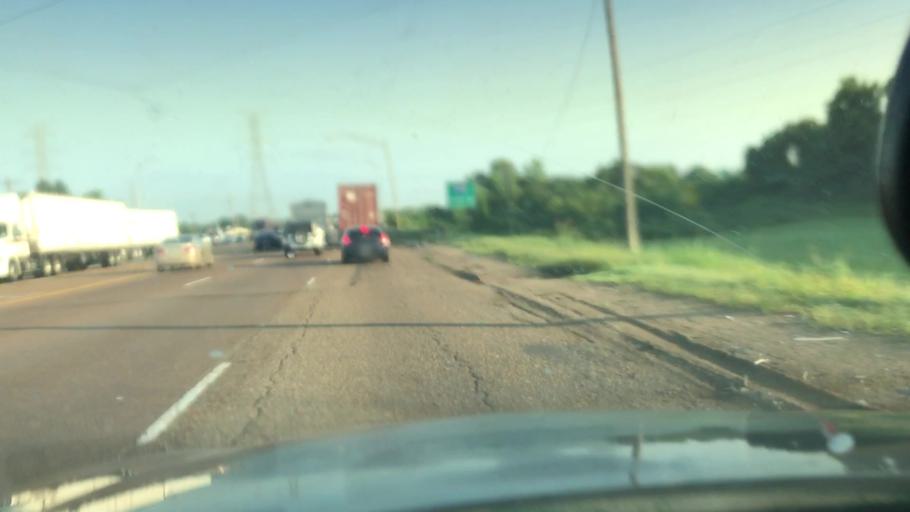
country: US
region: Tennessee
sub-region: Shelby County
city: New South Memphis
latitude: 35.0772
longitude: -89.9518
